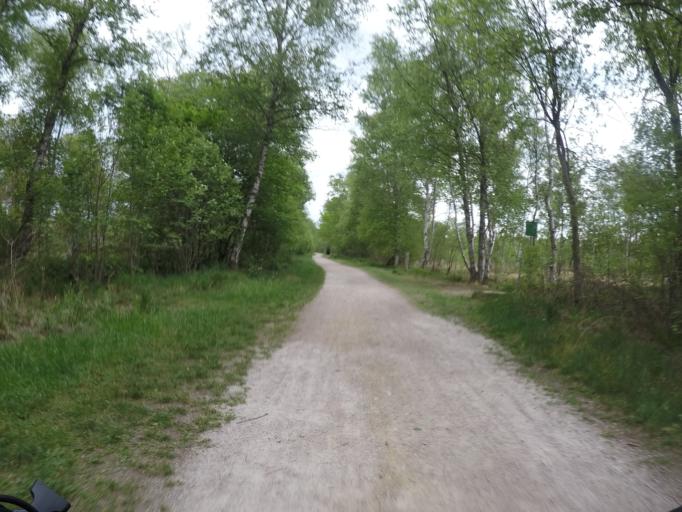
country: DE
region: Schleswig-Holstein
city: Henstedt-Ulzburg
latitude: 53.7535
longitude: 10.0131
